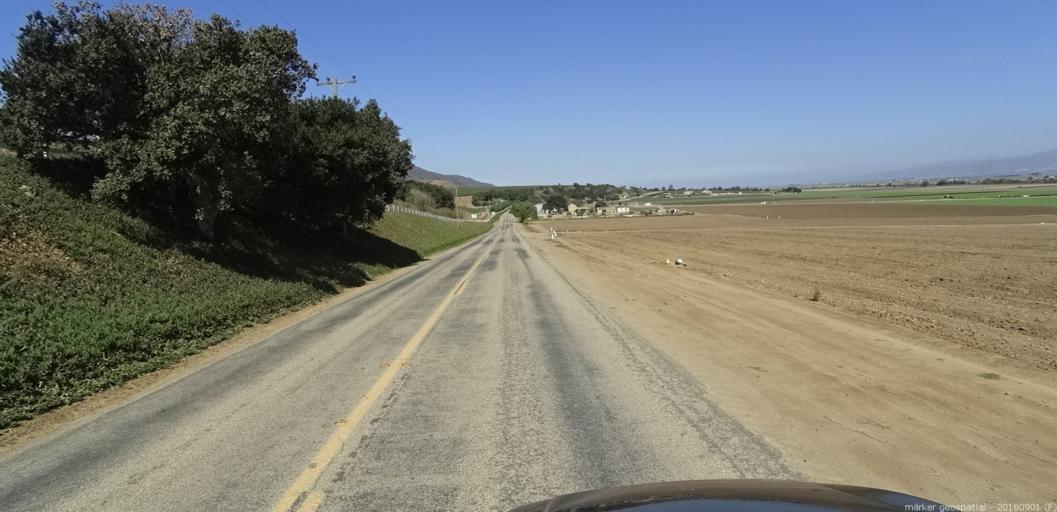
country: US
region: California
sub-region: Monterey County
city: Chualar
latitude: 36.5067
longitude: -121.5116
